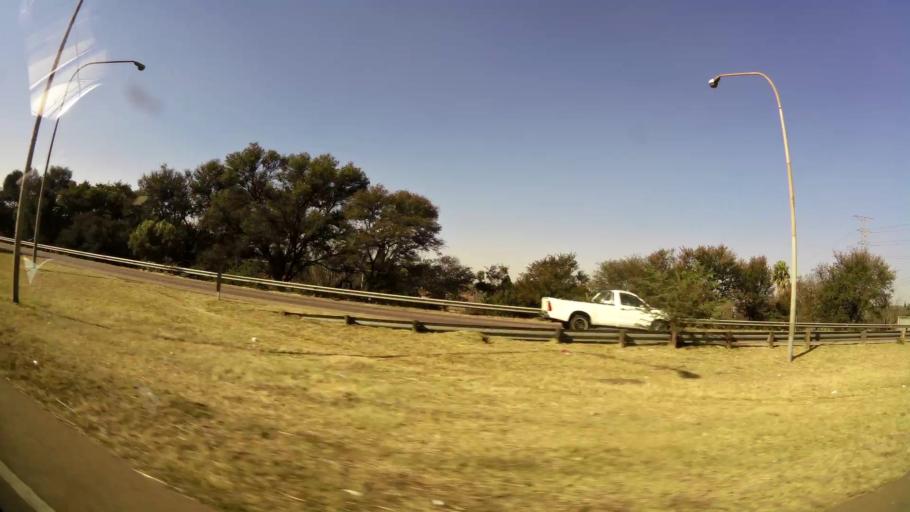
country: ZA
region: Gauteng
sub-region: City of Tshwane Metropolitan Municipality
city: Pretoria
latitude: -25.7230
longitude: 28.2581
